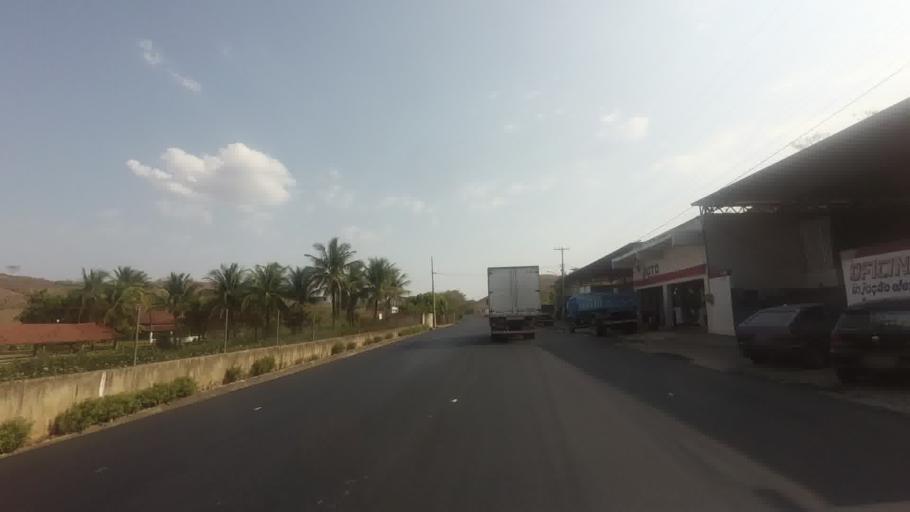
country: BR
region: Rio de Janeiro
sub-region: Bom Jesus Do Itabapoana
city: Bom Jesus do Itabapoana
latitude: -21.1446
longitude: -41.6652
